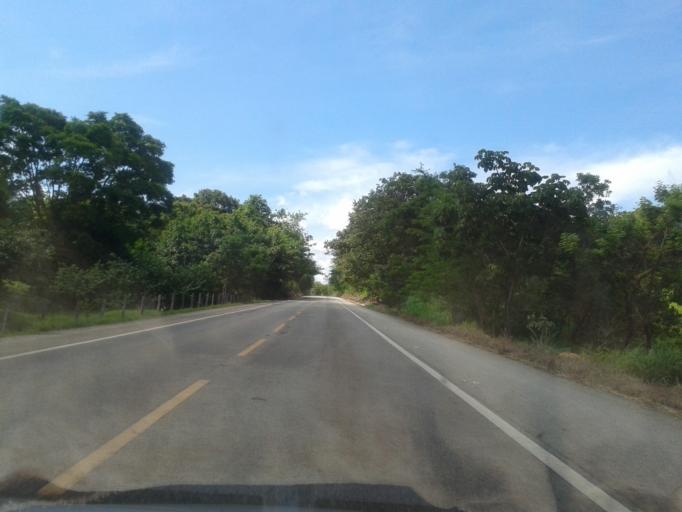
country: BR
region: Goias
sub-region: Goias
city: Goias
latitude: -15.6868
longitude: -50.2030
